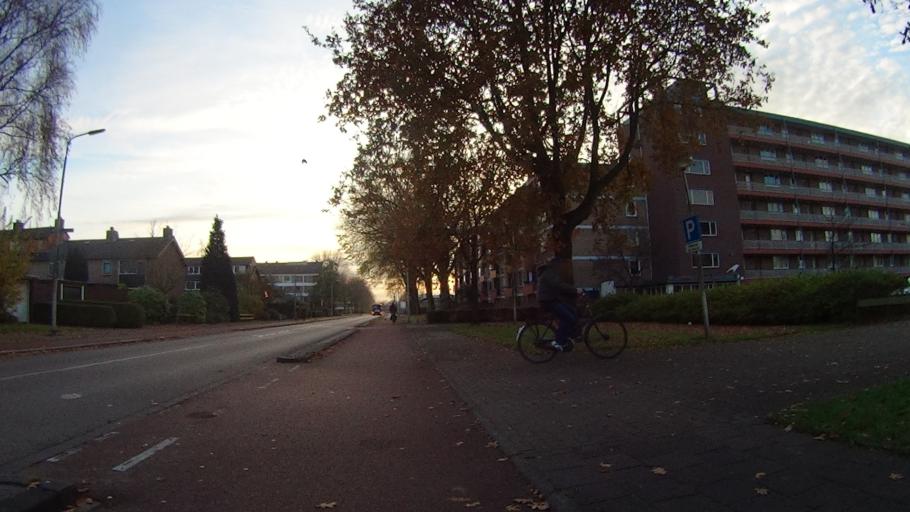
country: NL
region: Utrecht
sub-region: Gemeente Amersfoort
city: Randenbroek
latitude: 52.1704
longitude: 5.4041
